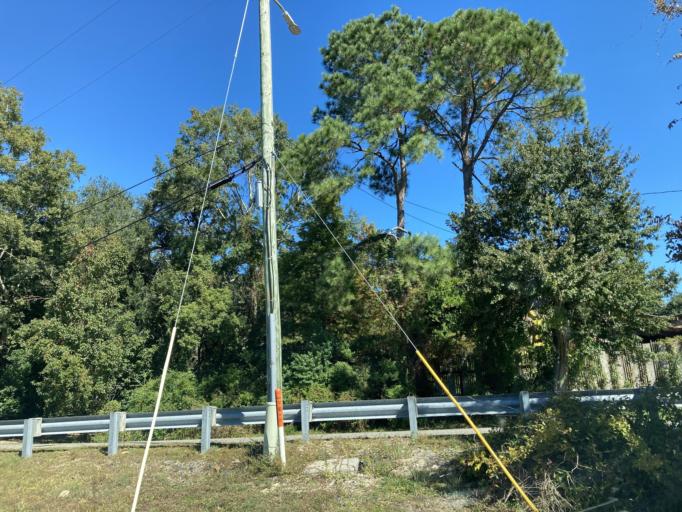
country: US
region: Mississippi
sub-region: Jackson County
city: Ocean Springs
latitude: 30.4062
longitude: -88.8222
